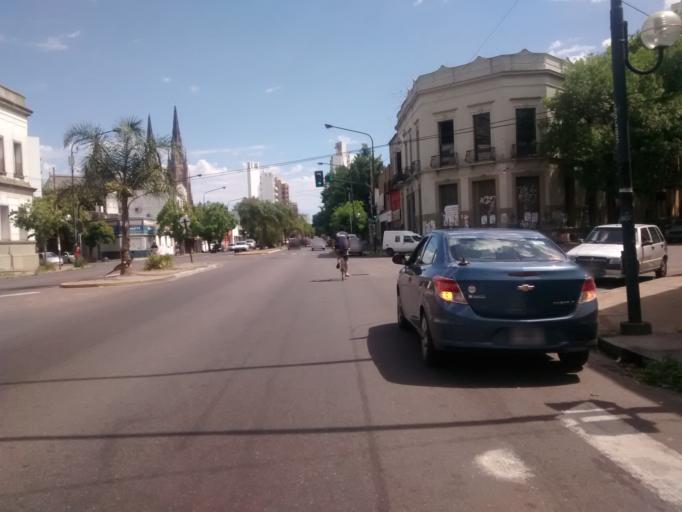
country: AR
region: Buenos Aires
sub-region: Partido de La Plata
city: La Plata
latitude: -34.9272
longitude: -57.9542
